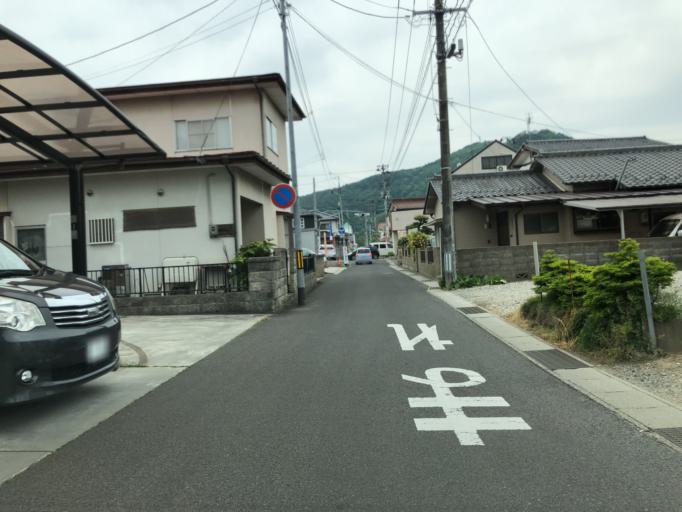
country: JP
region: Fukushima
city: Fukushima-shi
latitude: 37.7861
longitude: 140.4794
